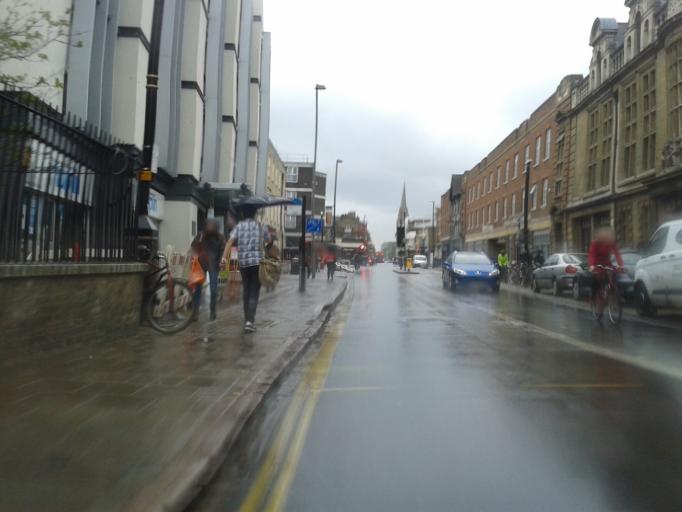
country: GB
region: England
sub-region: Cambridgeshire
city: Cambridge
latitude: 52.2028
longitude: 0.1242
